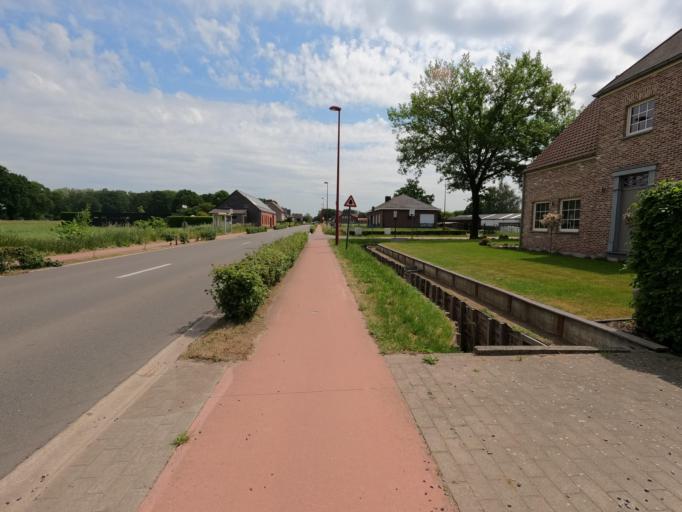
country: BE
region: Flanders
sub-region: Provincie Antwerpen
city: Olen
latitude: 51.1670
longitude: 4.9103
